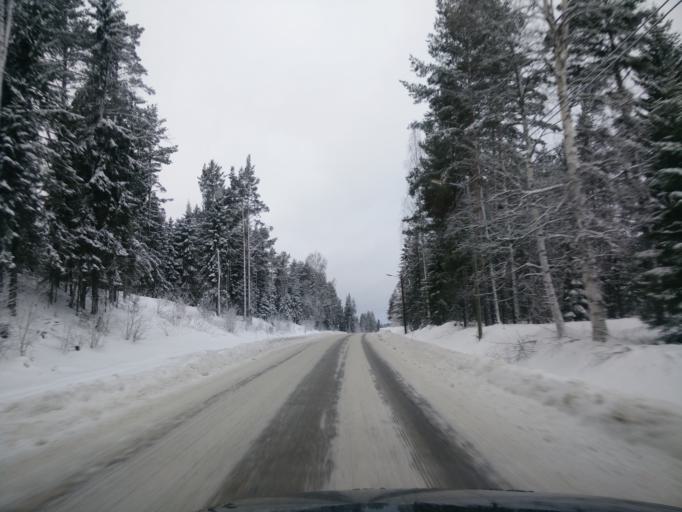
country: SE
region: Vaesternorrland
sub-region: Ange Kommun
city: Ange
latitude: 62.5022
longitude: 15.5164
